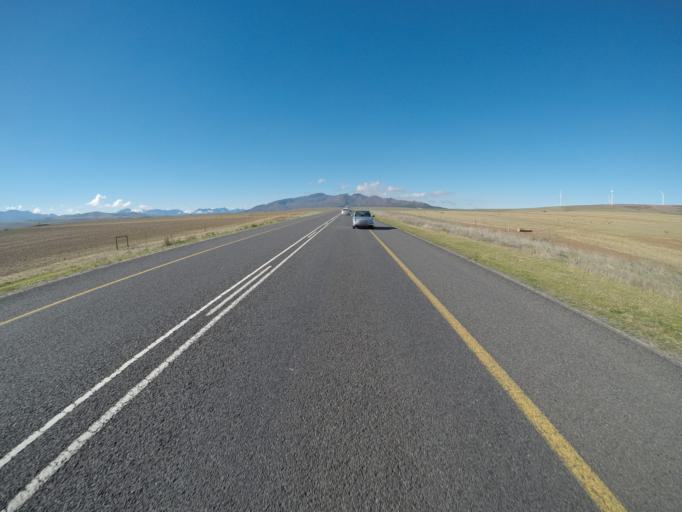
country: ZA
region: Western Cape
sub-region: Overberg District Municipality
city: Caledon
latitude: -34.2117
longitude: 19.3627
